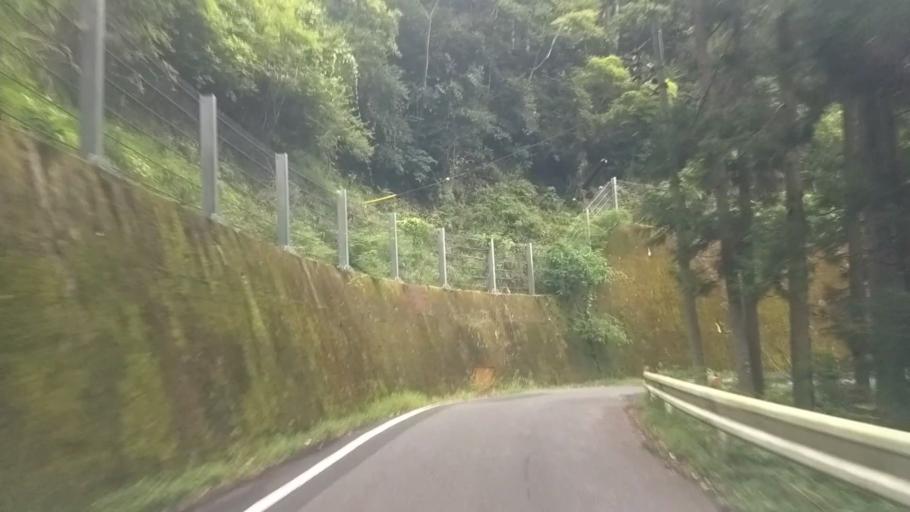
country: JP
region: Chiba
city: Kawaguchi
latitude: 35.1852
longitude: 140.1353
